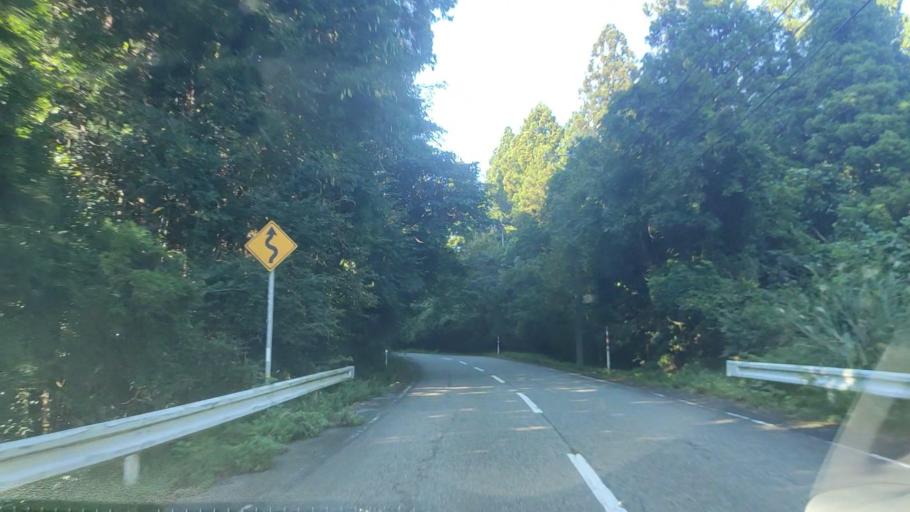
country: JP
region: Ishikawa
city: Nanao
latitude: 37.1098
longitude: 136.9618
